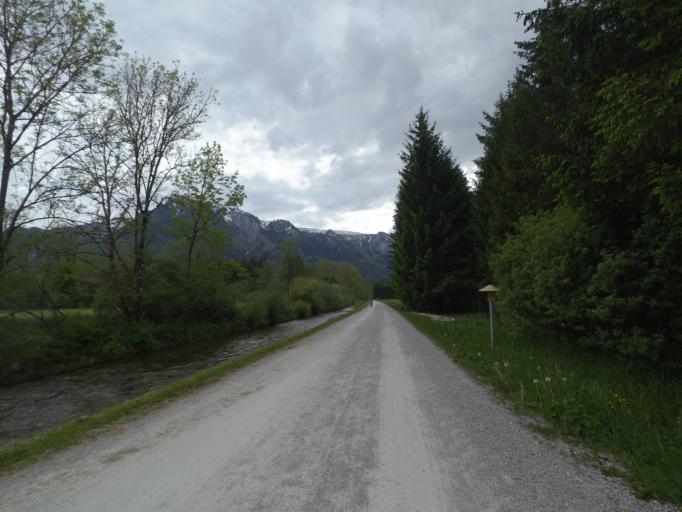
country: AT
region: Salzburg
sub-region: Politischer Bezirk Salzburg-Umgebung
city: Grodig
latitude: 47.7585
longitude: 12.9977
